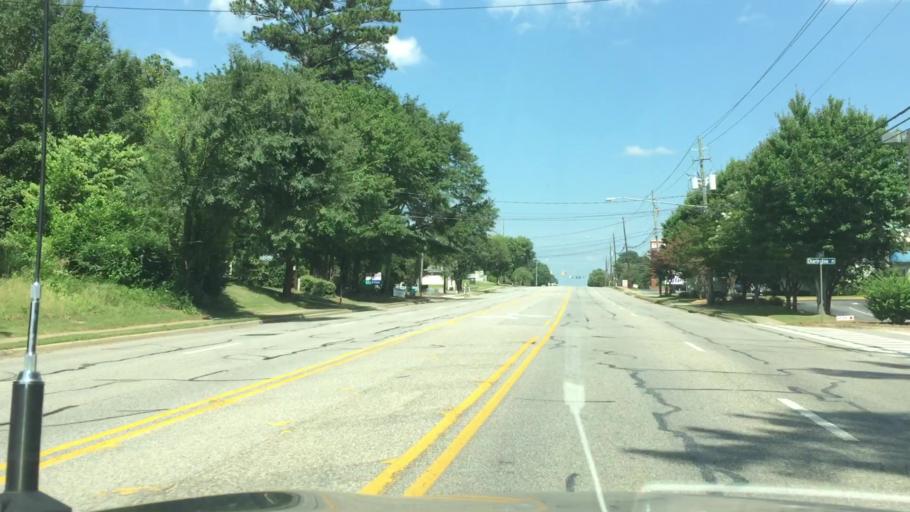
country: US
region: Alabama
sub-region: Lee County
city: Auburn
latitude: 32.6090
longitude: -85.4686
